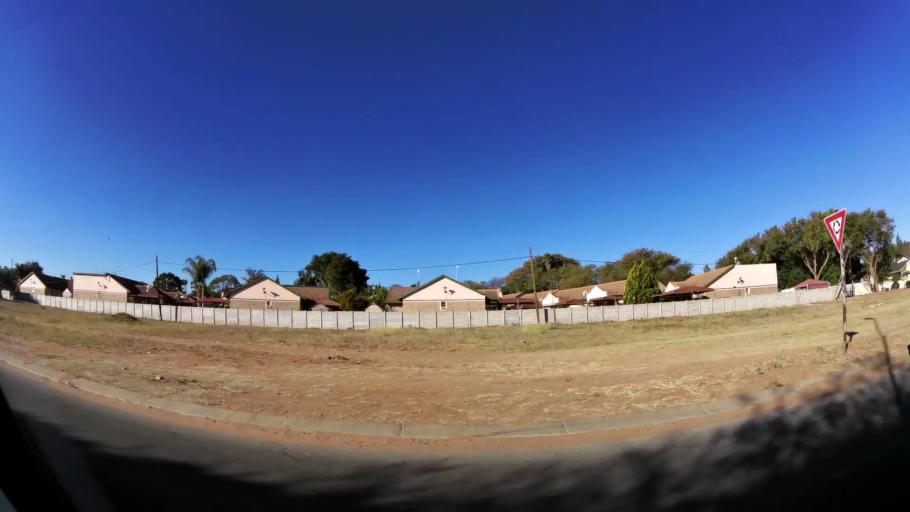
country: ZA
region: Limpopo
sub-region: Capricorn District Municipality
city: Polokwane
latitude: -23.8903
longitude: 29.4757
